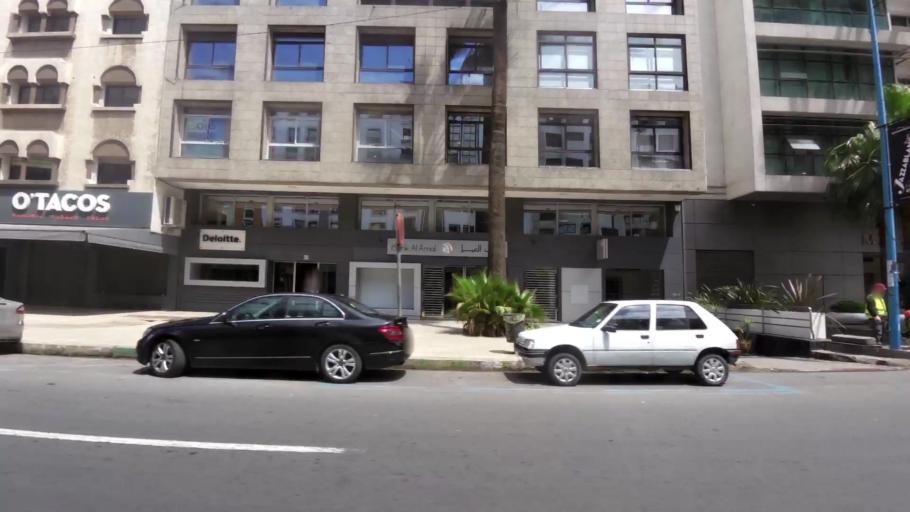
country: MA
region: Grand Casablanca
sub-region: Casablanca
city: Casablanca
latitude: 33.5921
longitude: -7.6367
